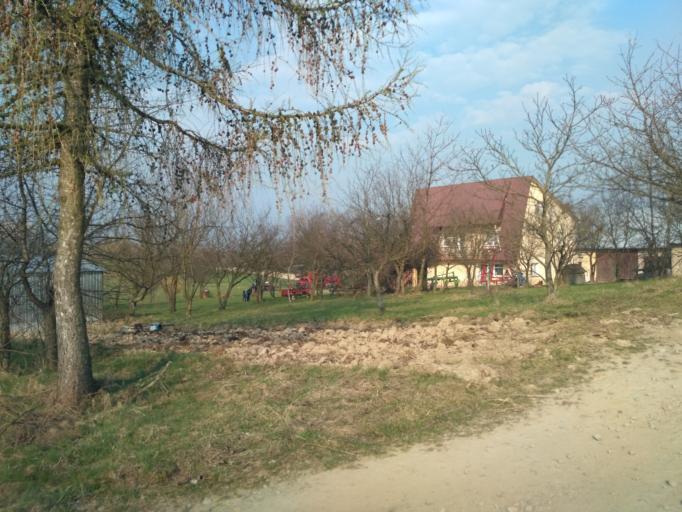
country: PL
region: Subcarpathian Voivodeship
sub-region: Powiat ropczycko-sedziszowski
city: Wielopole Skrzynskie
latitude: 49.9021
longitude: 21.5853
